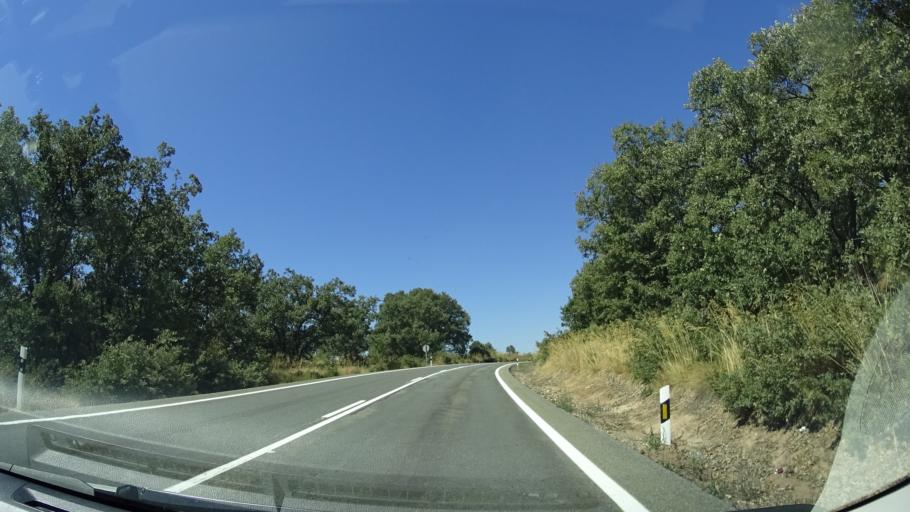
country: ES
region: Castille and Leon
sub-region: Provincia de Avila
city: Navalperal de Pinares
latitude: 40.5921
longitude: -4.4881
